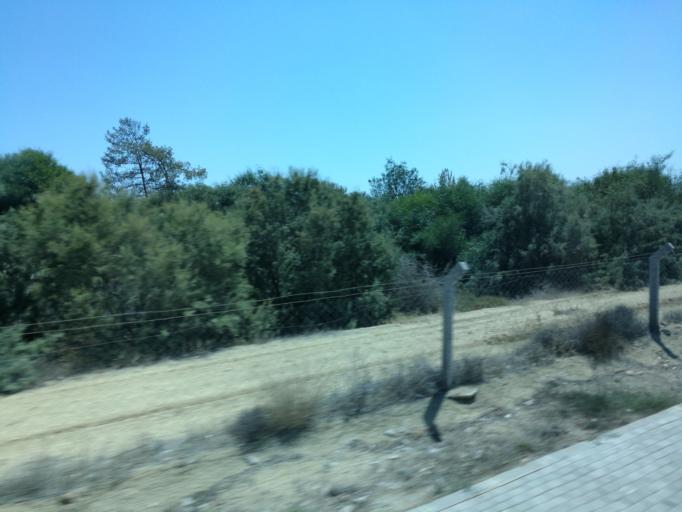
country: CY
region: Ammochostos
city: Famagusta
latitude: 35.1512
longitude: 33.9072
